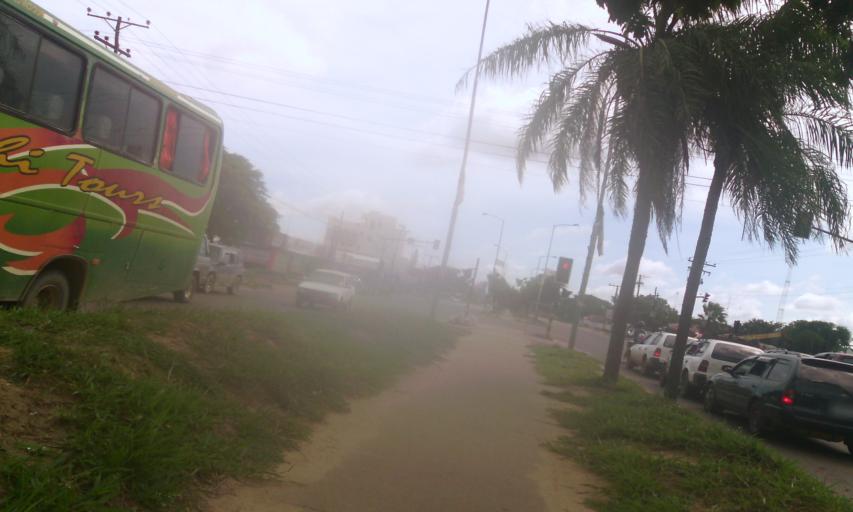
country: BO
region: Santa Cruz
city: Santa Cruz de la Sierra
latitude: -17.8167
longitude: -63.2137
